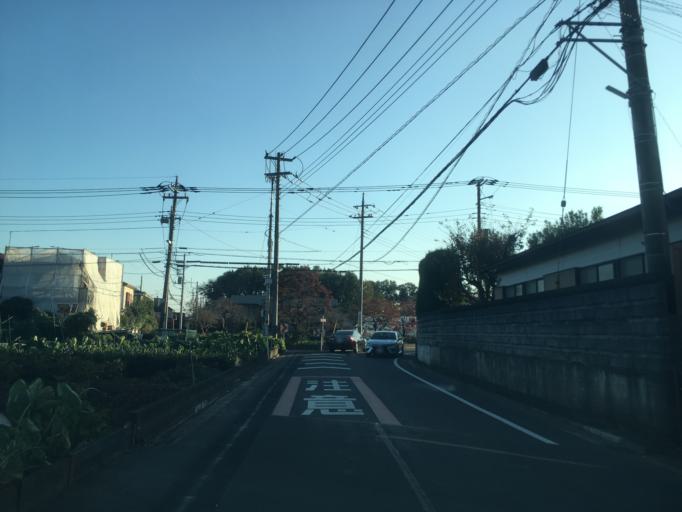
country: JP
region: Saitama
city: Tokorozawa
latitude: 35.8136
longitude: 139.4397
